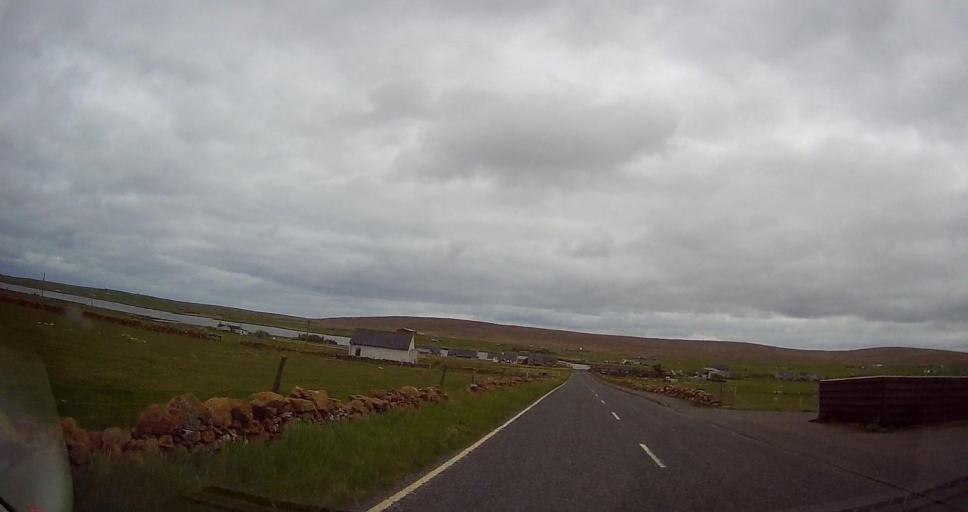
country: GB
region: Scotland
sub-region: Shetland Islands
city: Shetland
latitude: 60.7621
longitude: -0.8589
